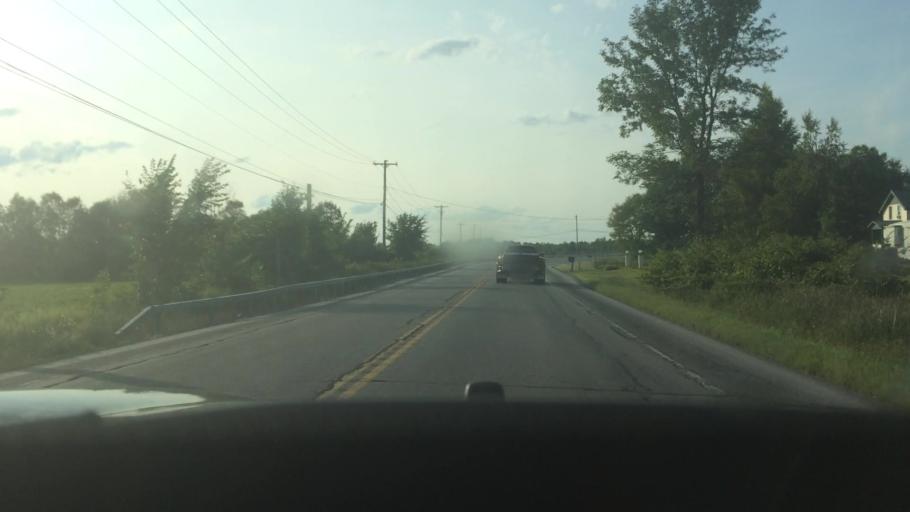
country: US
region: New York
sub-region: St. Lawrence County
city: Ogdensburg
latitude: 44.6813
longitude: -75.4440
